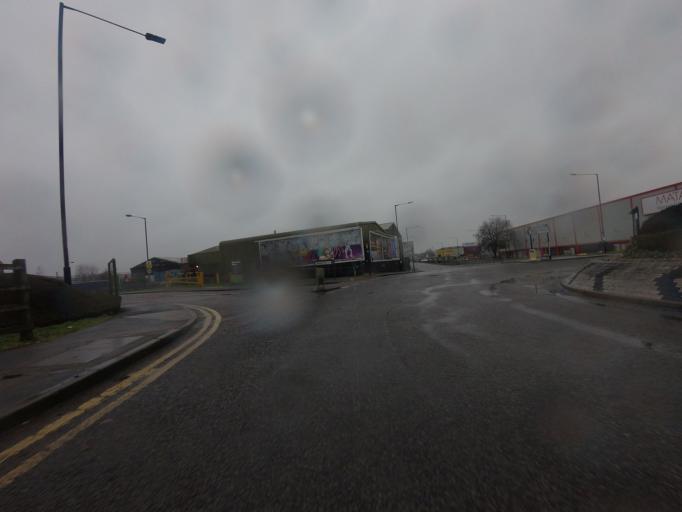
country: GB
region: England
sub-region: Hertfordshire
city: Waltham Cross
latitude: 51.6541
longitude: -0.0289
